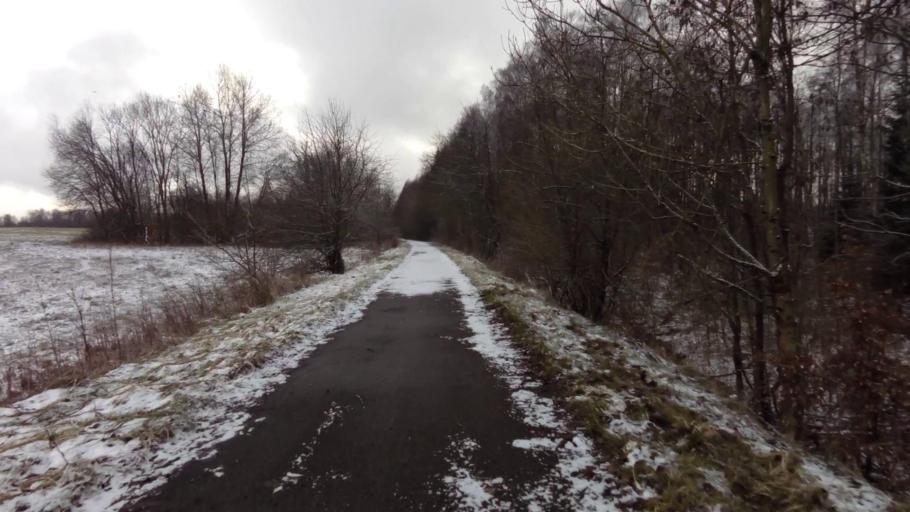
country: PL
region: West Pomeranian Voivodeship
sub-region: Powiat swidwinski
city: Polczyn-Zdroj
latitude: 53.7080
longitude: 16.0368
